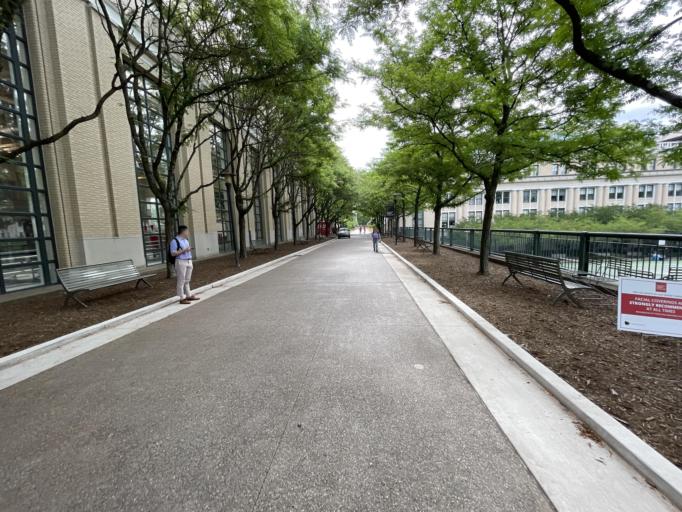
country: US
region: Pennsylvania
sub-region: Allegheny County
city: Bloomfield
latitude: 40.4428
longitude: -79.9421
